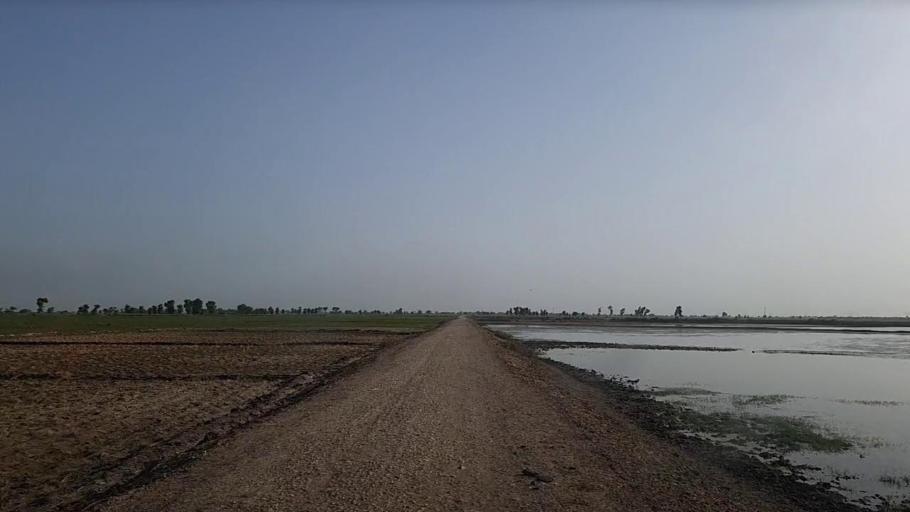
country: PK
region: Sindh
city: Sita Road
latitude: 27.1054
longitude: 67.8889
